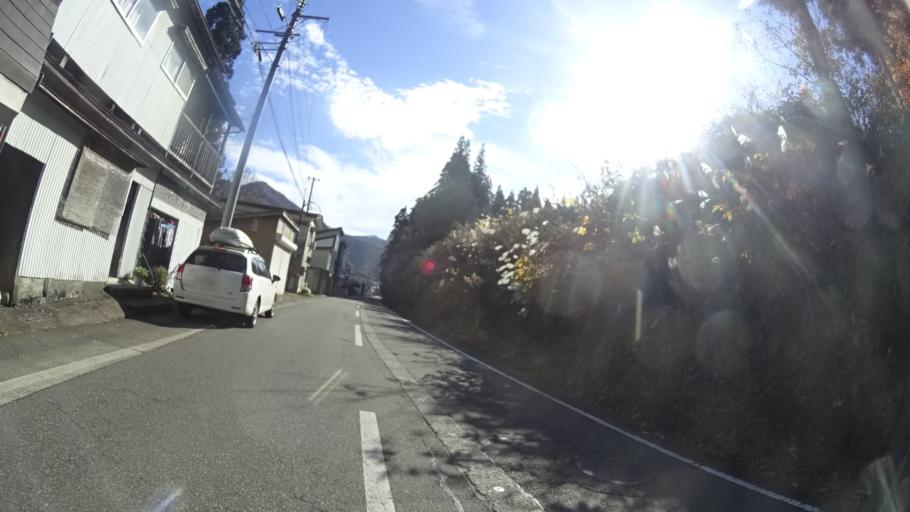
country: JP
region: Niigata
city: Muikamachi
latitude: 37.1960
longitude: 139.0774
